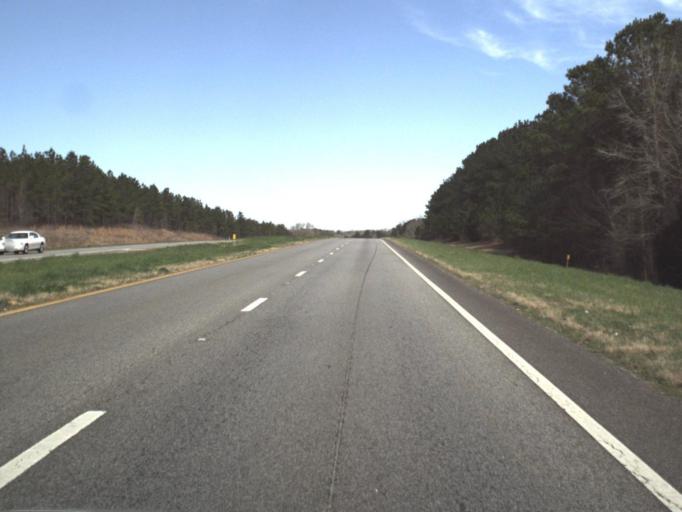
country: US
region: Florida
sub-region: Jackson County
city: Marianna
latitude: 30.8318
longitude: -85.3551
